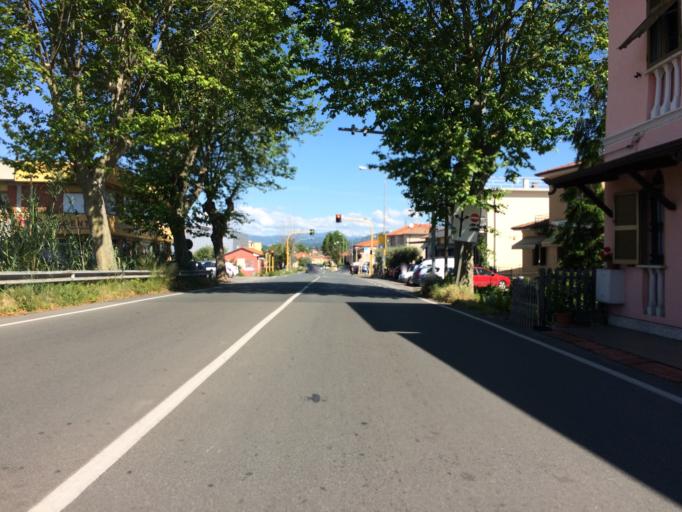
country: IT
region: Liguria
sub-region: Provincia di La Spezia
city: Colombiera-Molicciara
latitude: 44.0821
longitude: 10.0088
